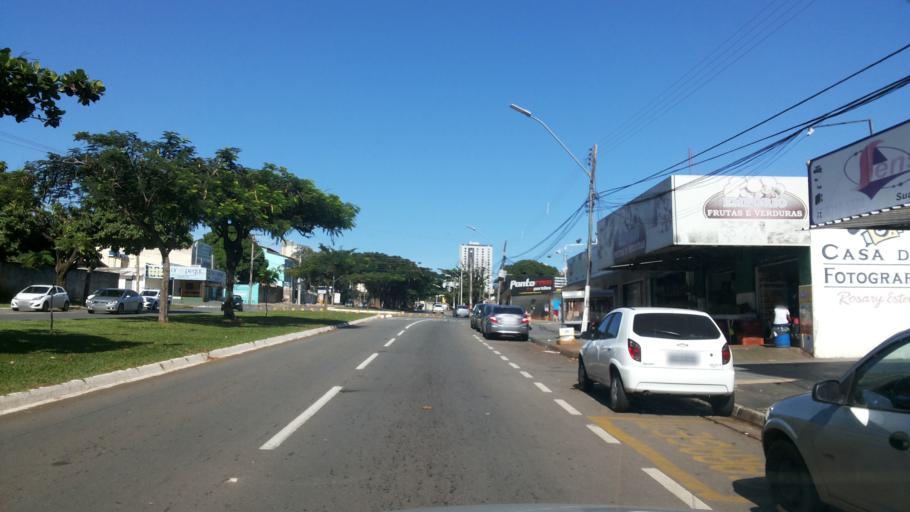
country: BR
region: Goias
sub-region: Goiania
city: Goiania
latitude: -16.7058
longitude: -49.2492
